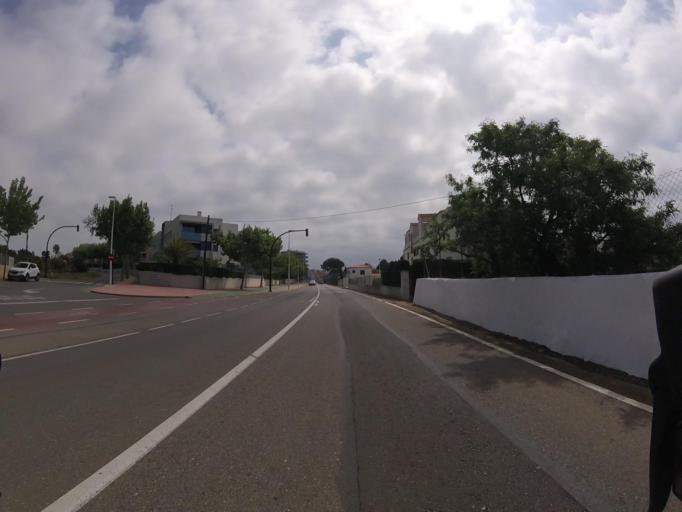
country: ES
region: Valencia
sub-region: Provincia de Castello
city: Alcoceber
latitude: 40.2443
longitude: 0.2709
